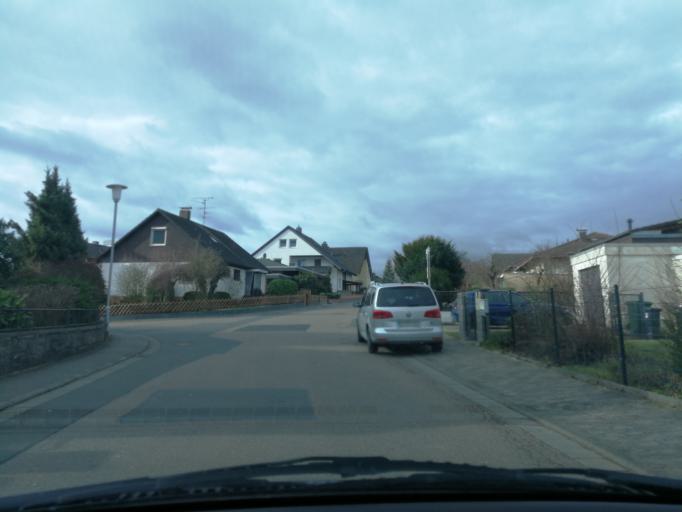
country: DE
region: Hesse
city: Reinheim
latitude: 49.8234
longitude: 8.8277
